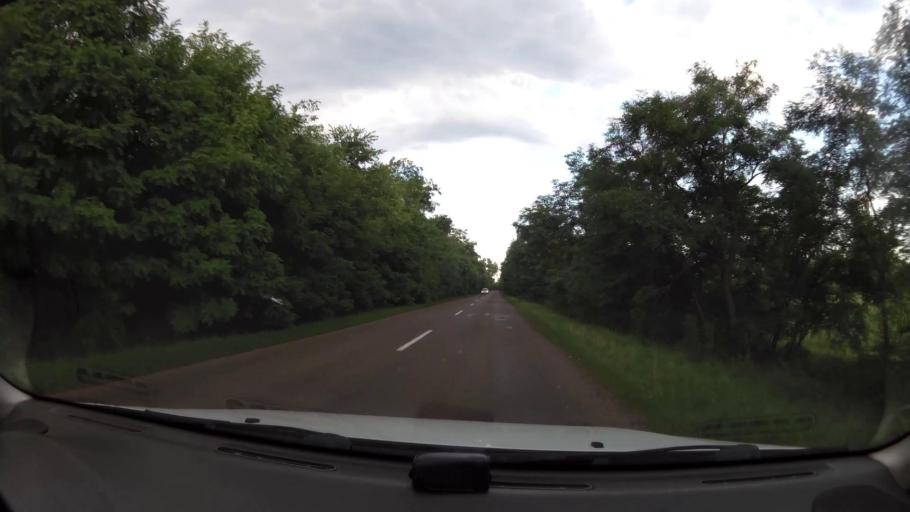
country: HU
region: Pest
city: Tapiosag
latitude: 47.3896
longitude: 19.6461
